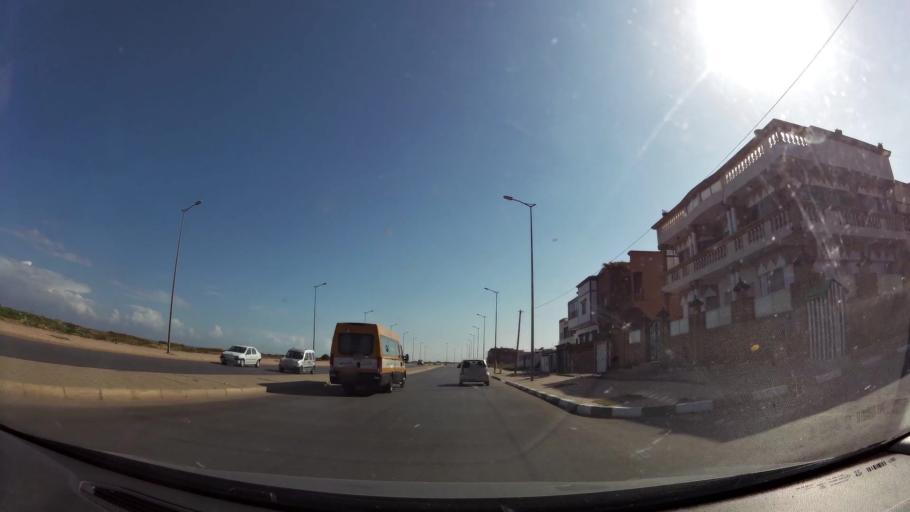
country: MA
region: Rabat-Sale-Zemmour-Zaer
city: Sale
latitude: 34.0711
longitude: -6.8028
